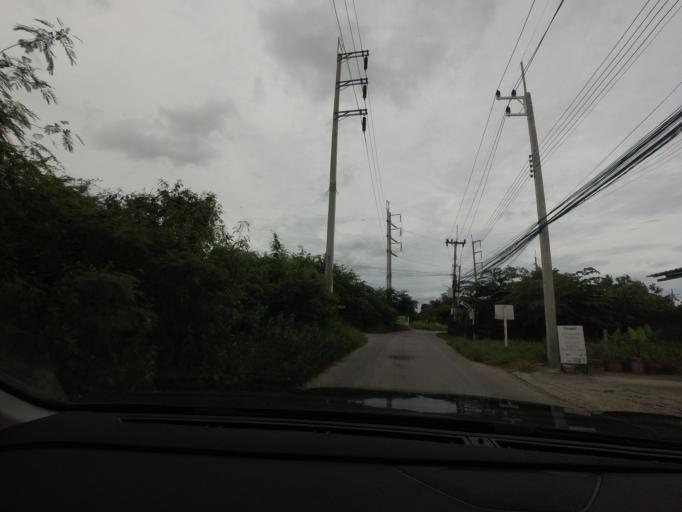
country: TH
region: Prachuap Khiri Khan
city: Hua Hin
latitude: 12.5379
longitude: 99.9506
